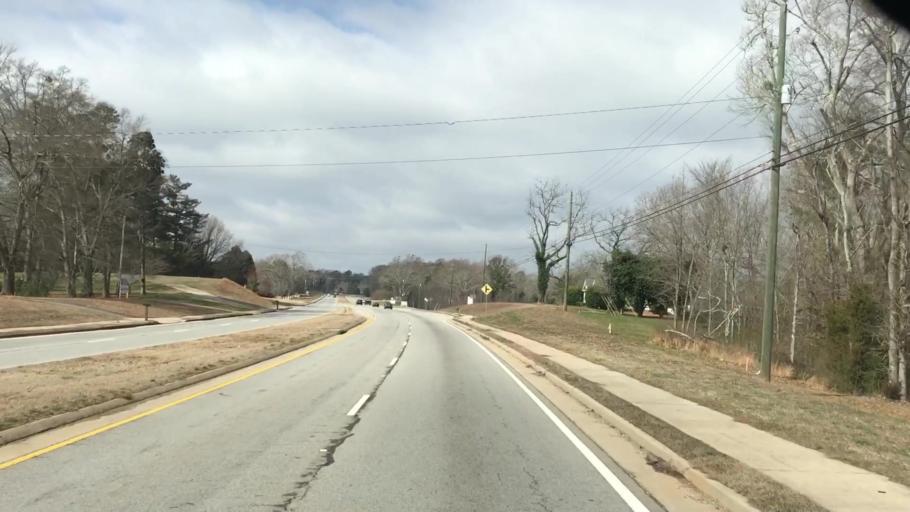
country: US
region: Georgia
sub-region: Hall County
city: Oakwood
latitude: 34.1785
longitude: -83.8428
